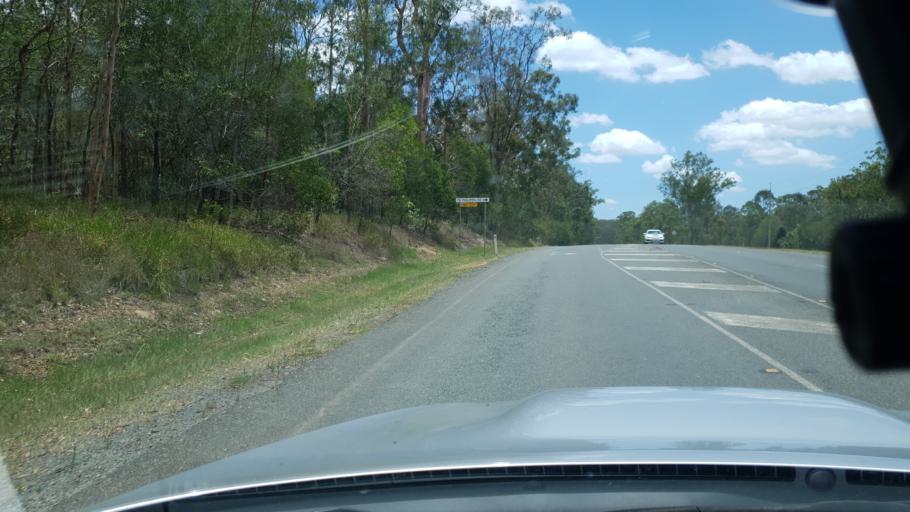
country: AU
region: Queensland
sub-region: Logan
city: North Maclean
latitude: -27.7657
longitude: 152.9847
